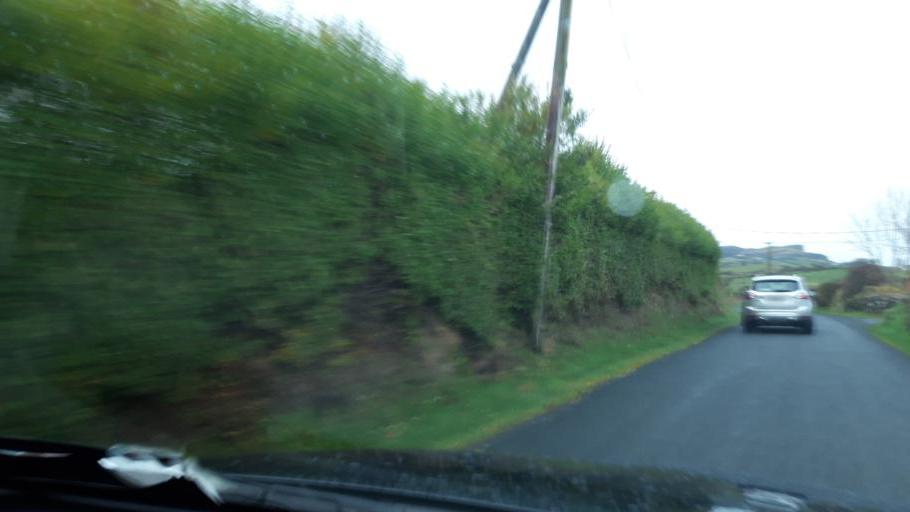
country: IE
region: Ulster
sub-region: County Donegal
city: Buncrana
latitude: 55.2387
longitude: -7.6191
